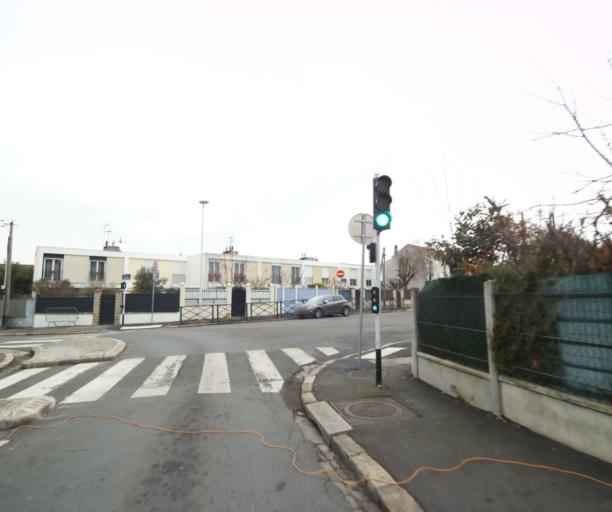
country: FR
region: Ile-de-France
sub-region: Departement des Hauts-de-Seine
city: Nanterre
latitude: 48.8804
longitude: 2.2025
